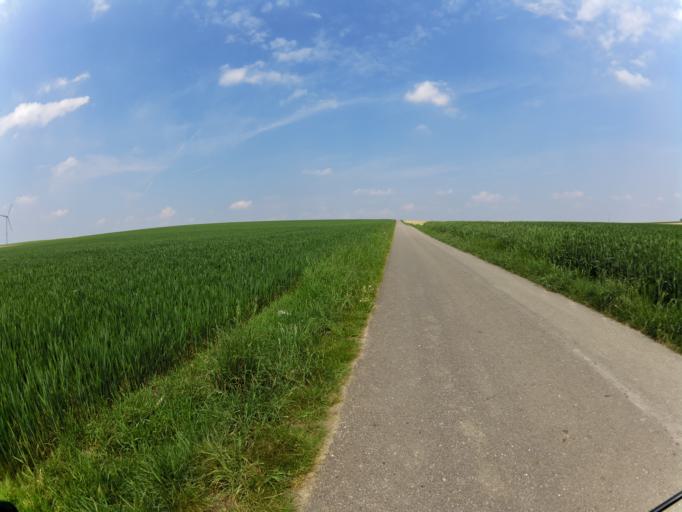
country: DE
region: North Rhine-Westphalia
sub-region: Regierungsbezirk Koln
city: Gangelt
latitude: 50.9917
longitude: 6.0225
